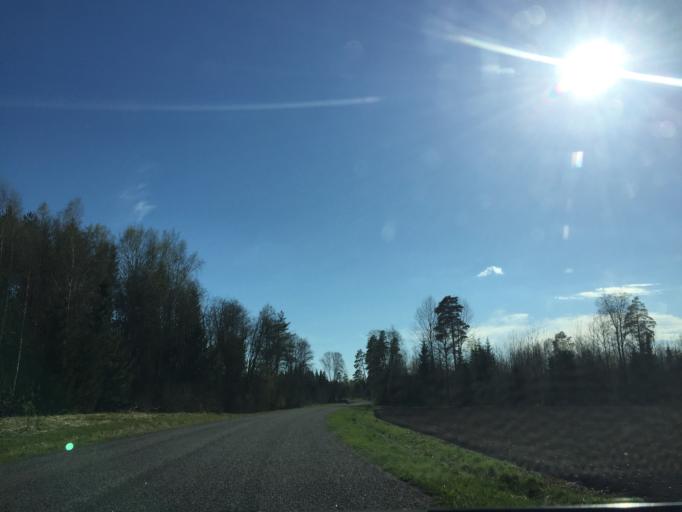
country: EE
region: Valgamaa
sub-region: Valga linn
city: Valga
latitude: 57.8497
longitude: 26.2522
